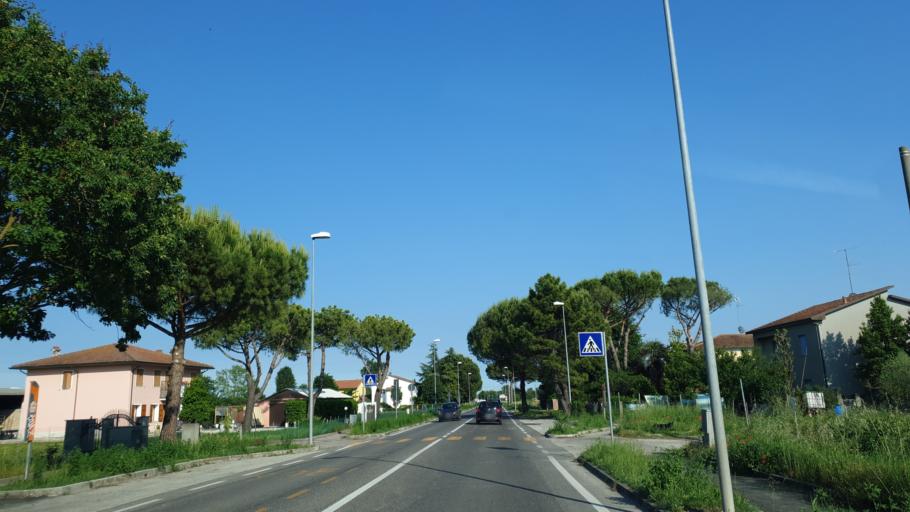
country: IT
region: Emilia-Romagna
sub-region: Provincia di Ravenna
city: Porto Fuori
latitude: 44.4091
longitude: 12.2326
